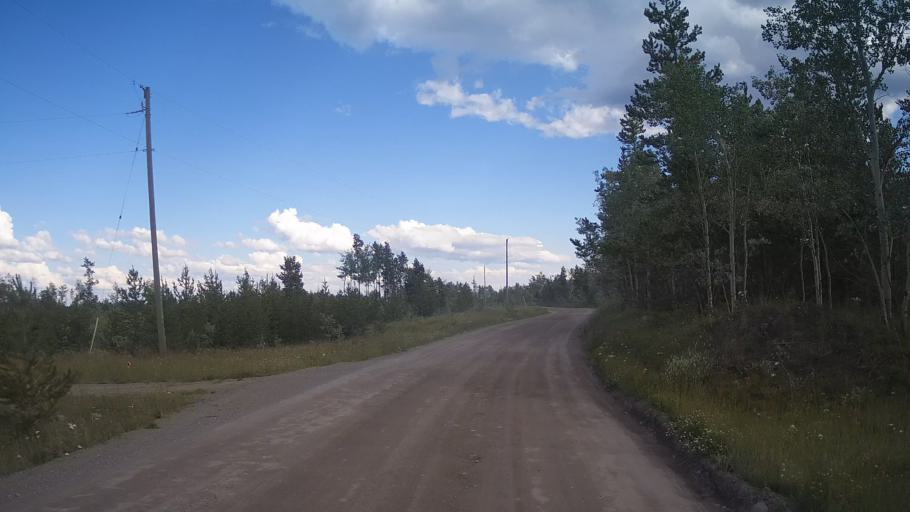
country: CA
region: British Columbia
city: Cache Creek
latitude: 51.2536
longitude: -121.6752
